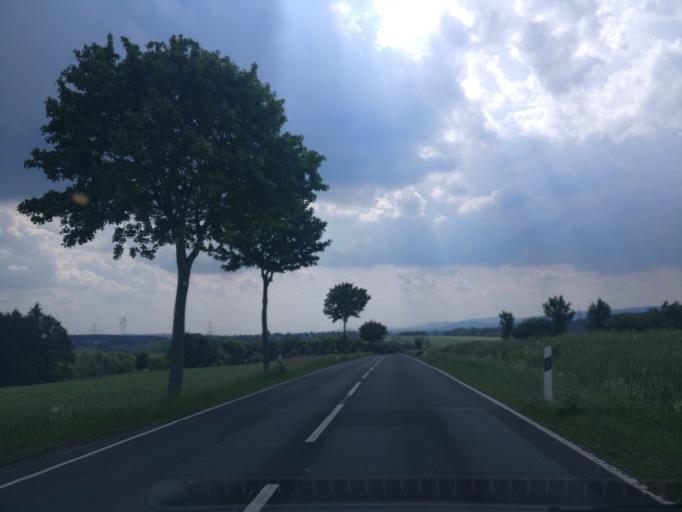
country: DE
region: Hesse
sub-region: Regierungsbezirk Kassel
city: Fuldatal
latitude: 51.3687
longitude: 9.6077
